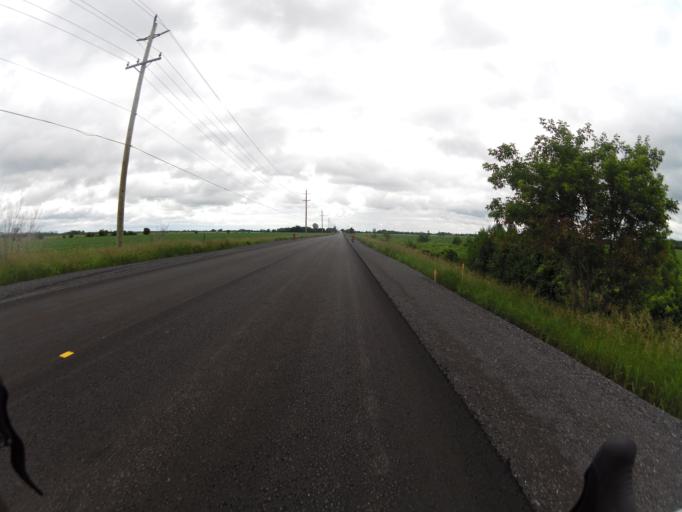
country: CA
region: Ontario
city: Bells Corners
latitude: 45.2457
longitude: -75.8828
